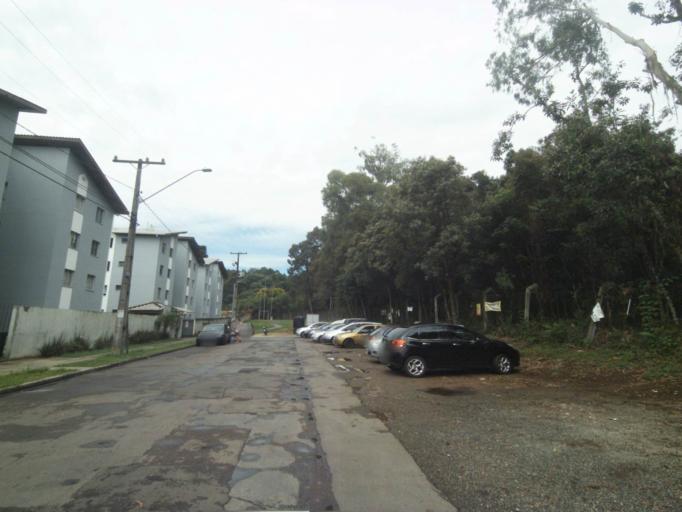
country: BR
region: Parana
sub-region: Pinhais
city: Pinhais
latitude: -25.4723
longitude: -49.2022
